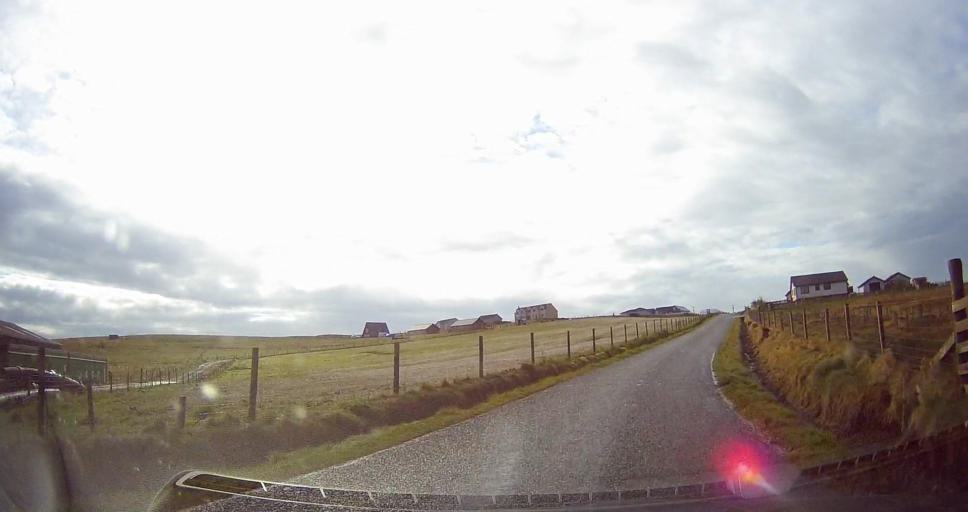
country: GB
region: Scotland
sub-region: Shetland Islands
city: Sandwick
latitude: 60.0600
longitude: -1.2160
